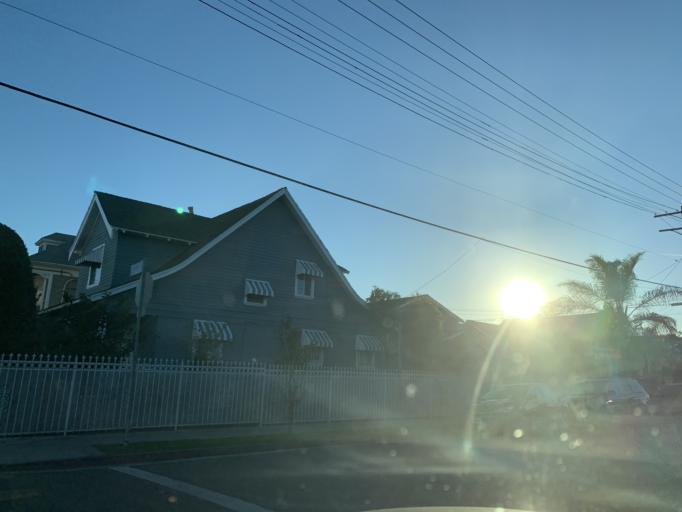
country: US
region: California
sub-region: Los Angeles County
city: Silver Lake
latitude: 34.0492
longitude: -118.2969
